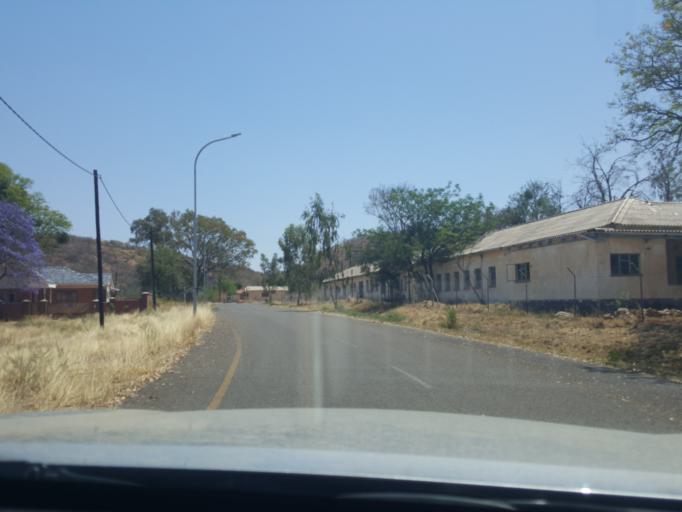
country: BW
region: South East
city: Lobatse
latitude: -25.1916
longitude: 25.6750
